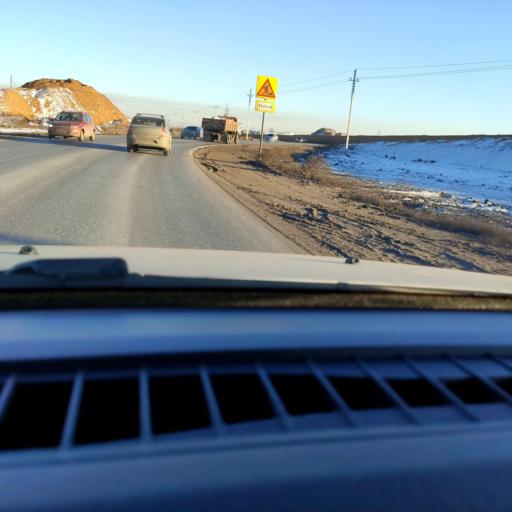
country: RU
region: Samara
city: Podstepki
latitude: 53.5618
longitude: 49.1974
